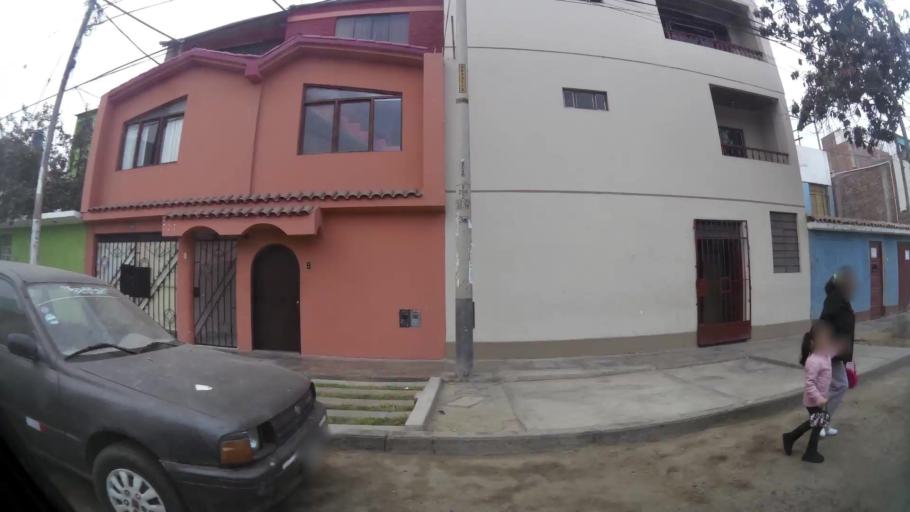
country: PE
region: La Libertad
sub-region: Provincia de Trujillo
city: Trujillo
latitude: -8.0954
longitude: -79.0217
